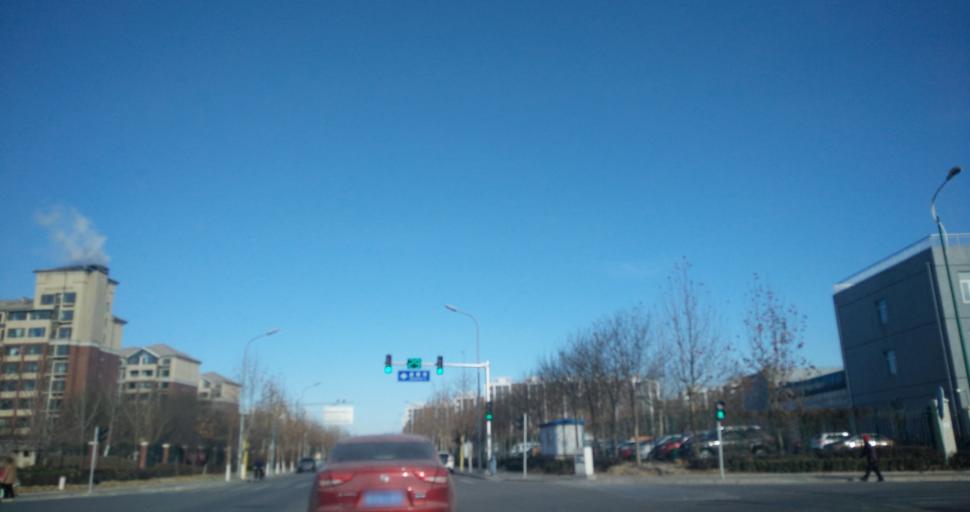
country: CN
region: Beijing
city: Yinghai
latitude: 39.7121
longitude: 116.3971
